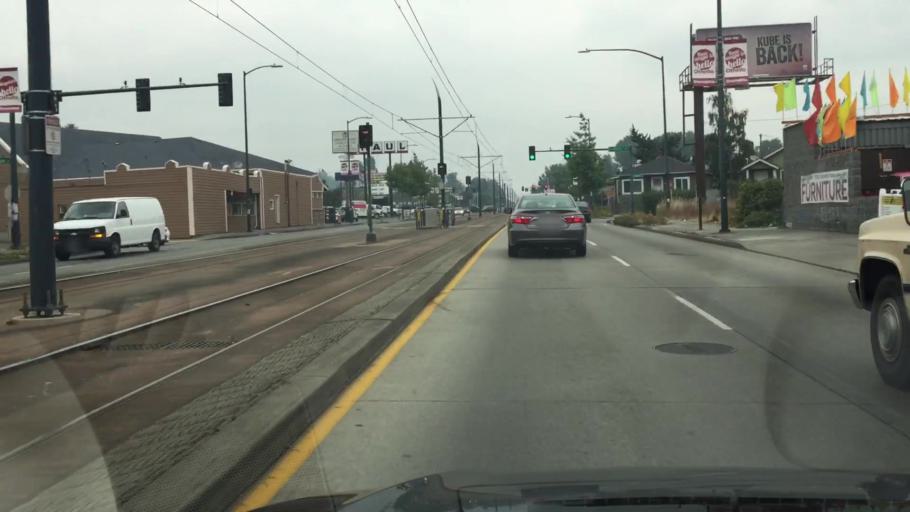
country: US
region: Washington
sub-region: King County
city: Riverton
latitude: 47.5439
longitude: -122.2845
